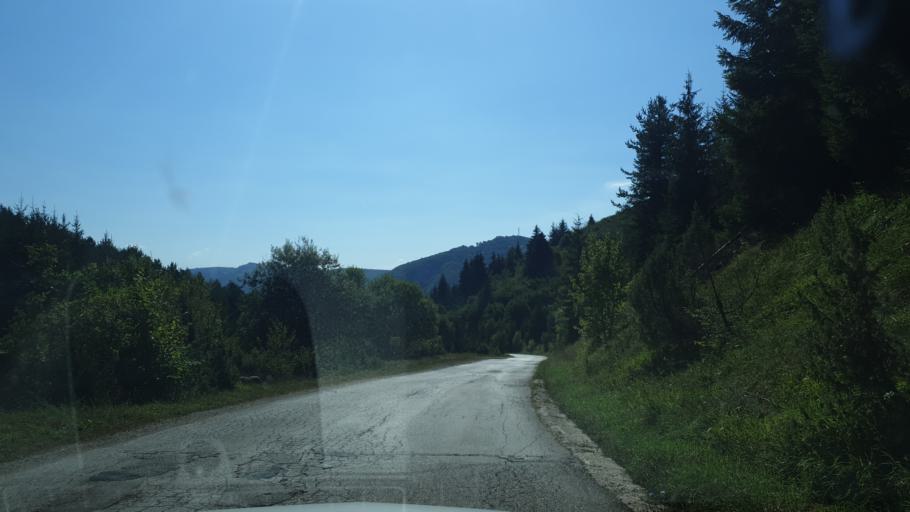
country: RS
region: Central Serbia
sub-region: Zlatiborski Okrug
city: Nova Varos
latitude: 43.4246
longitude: 19.9207
